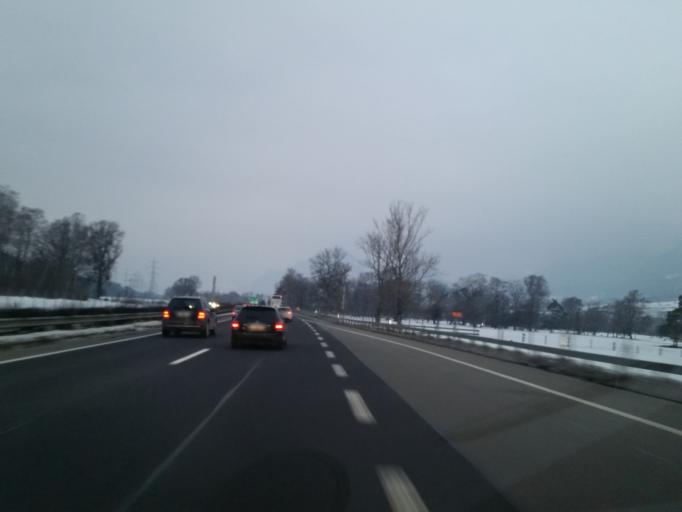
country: CH
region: Grisons
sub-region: Landquart District
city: Malans
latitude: 46.9753
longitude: 9.5504
